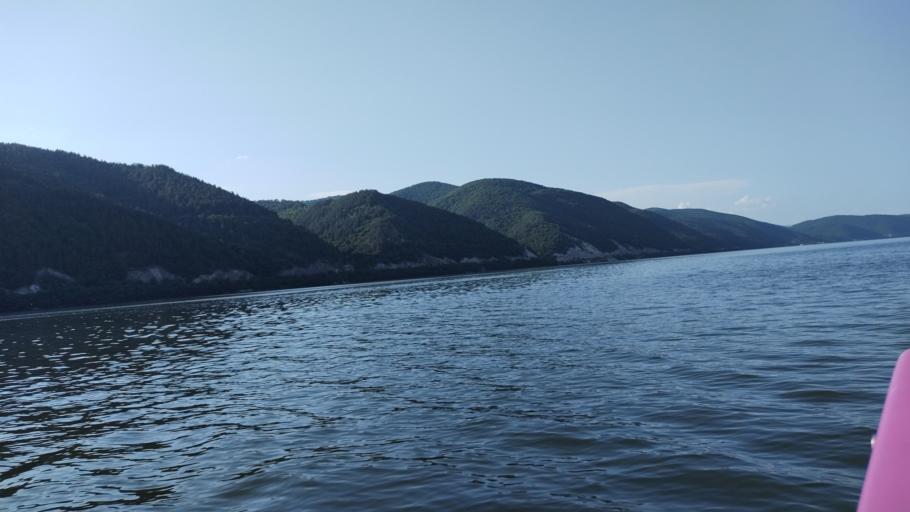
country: RO
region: Mehedinti
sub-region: Comuna Dubova
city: Dubova
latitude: 44.5300
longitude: 22.2119
